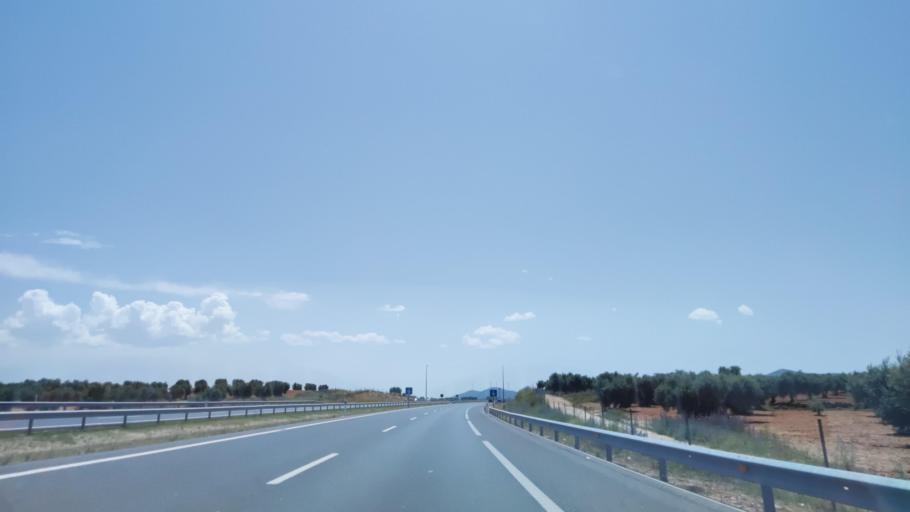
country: ES
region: Castille-La Mancha
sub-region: Province of Toledo
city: Nambroca
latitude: 39.8008
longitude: -3.9620
